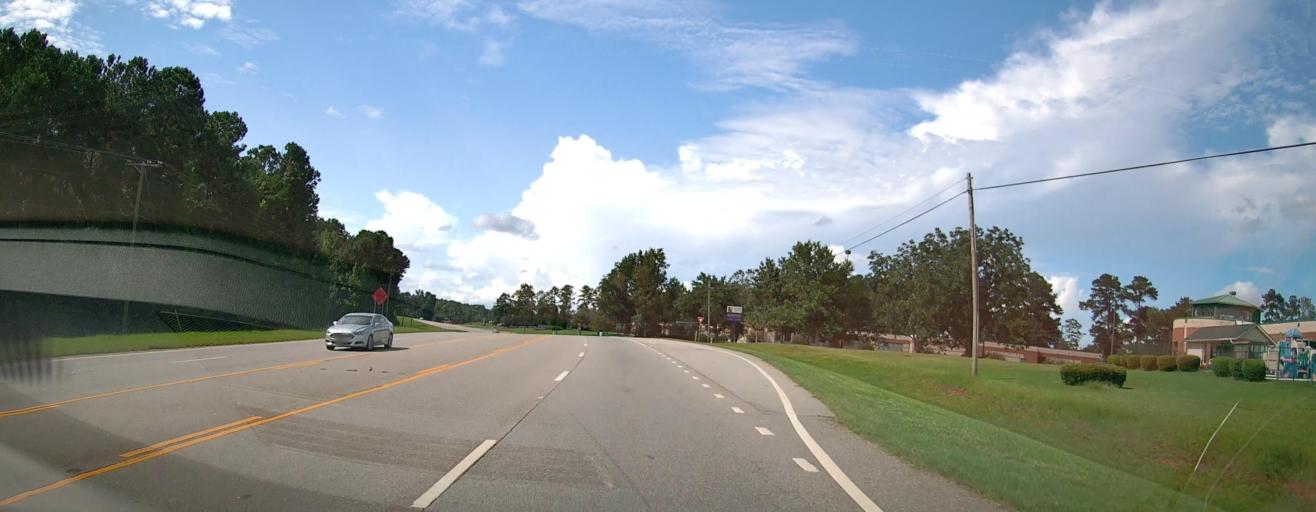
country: US
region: Georgia
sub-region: Upson County
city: Thomaston
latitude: 32.8609
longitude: -84.3181
